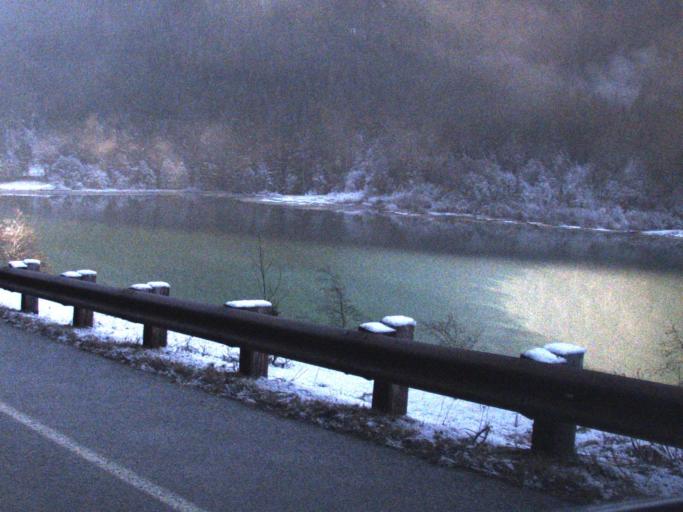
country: US
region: Washington
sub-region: Snohomish County
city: Darrington
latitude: 48.6960
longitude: -121.0952
